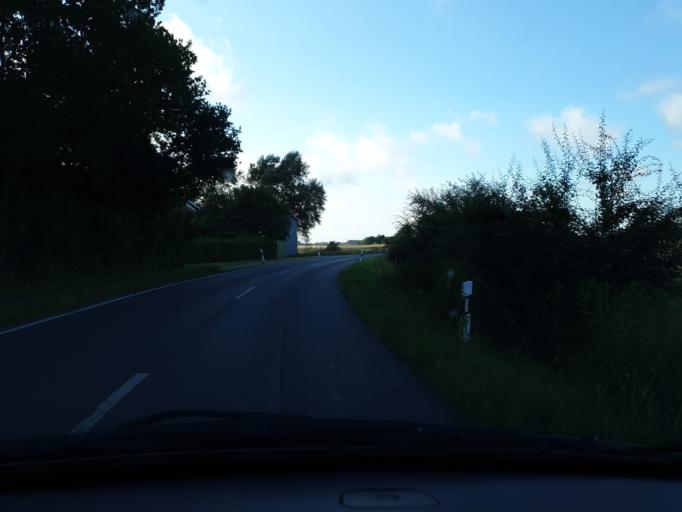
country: DE
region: Schleswig-Holstein
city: Wesselburener Deichhausen
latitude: 54.1460
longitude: 8.9164
